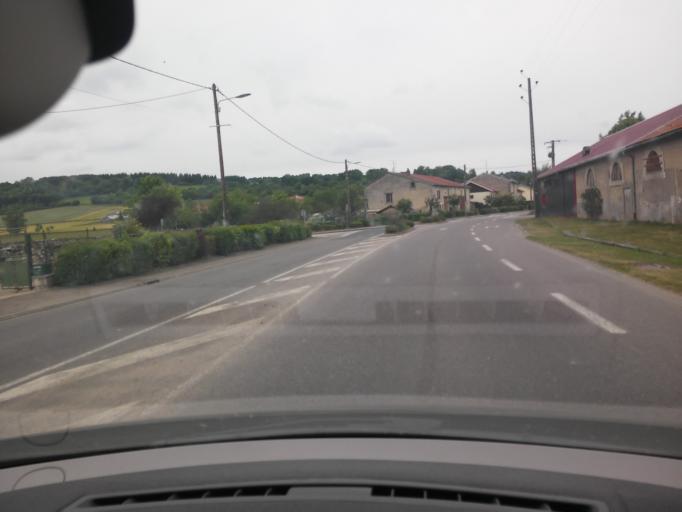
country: FR
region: Lorraine
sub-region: Departement de la Meuse
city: Lerouville
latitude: 48.8214
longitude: 5.5119
